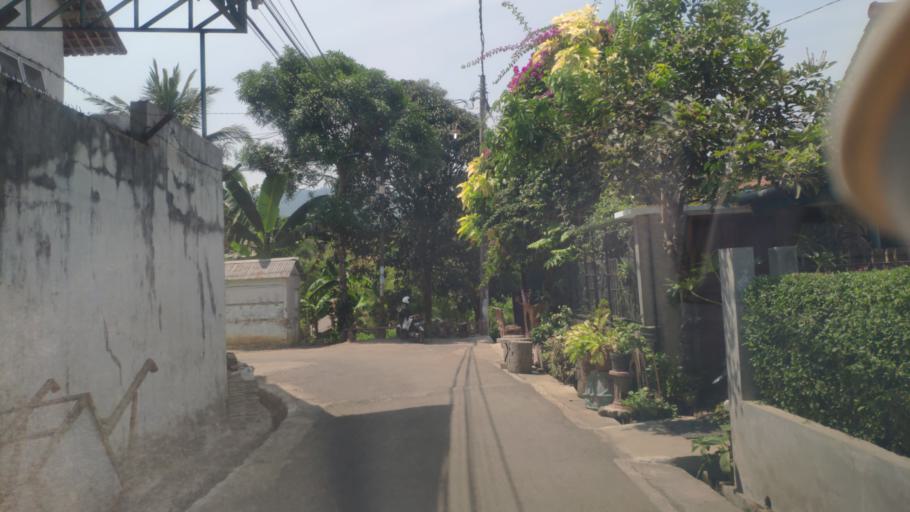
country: ID
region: Central Java
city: Wonosobo
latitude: -7.3981
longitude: 109.6984
